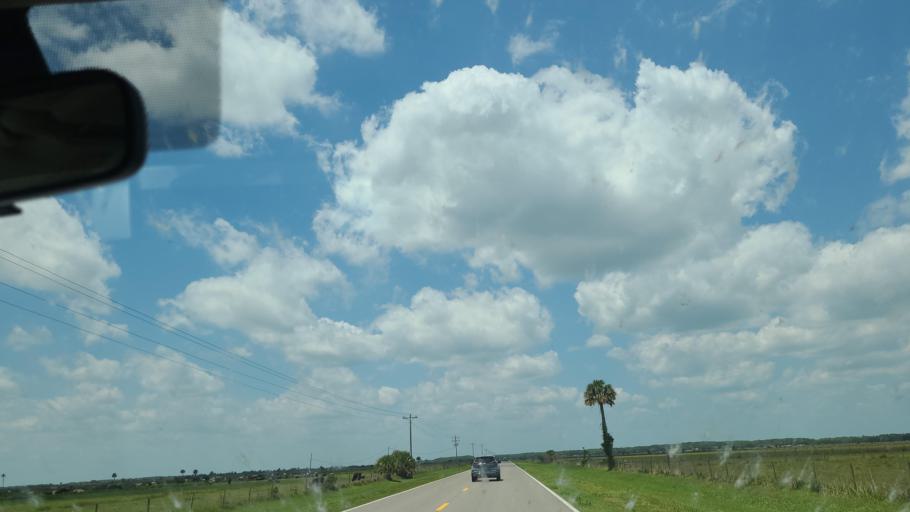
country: US
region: Florida
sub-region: Okeechobee County
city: Okeechobee
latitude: 27.3886
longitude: -80.9373
